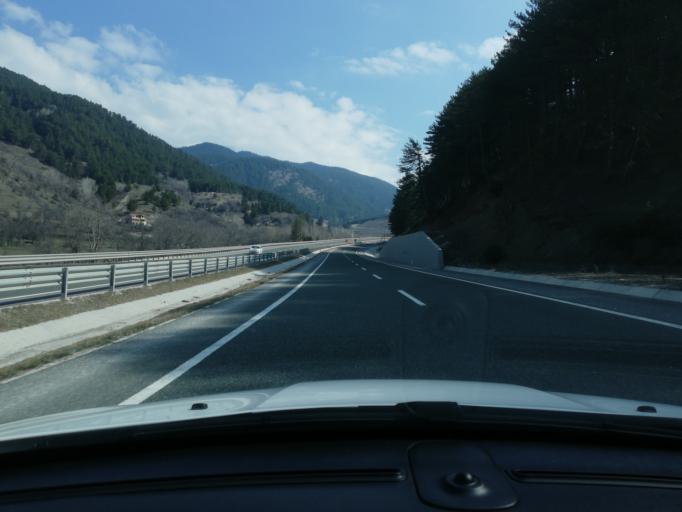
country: TR
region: Cankiri
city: Ilgaz
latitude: 41.0296
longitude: 33.7365
